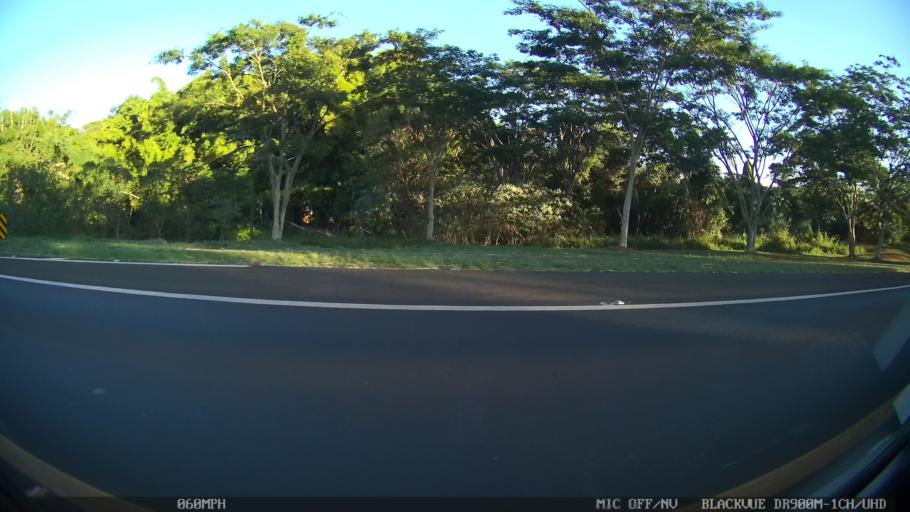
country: BR
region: Sao Paulo
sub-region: Araraquara
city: Araraquara
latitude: -21.8173
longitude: -48.1901
